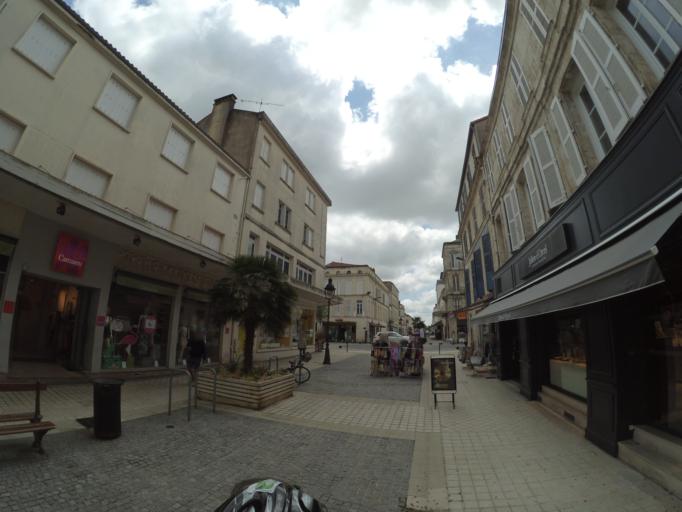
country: FR
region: Poitou-Charentes
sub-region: Departement de la Charente-Maritime
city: Rochefort
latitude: 45.9357
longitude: -0.9613
